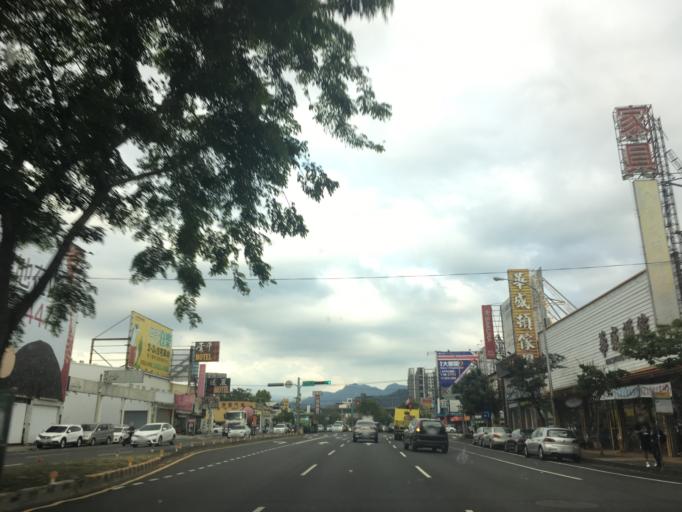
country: TW
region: Taiwan
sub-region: Taichung City
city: Taichung
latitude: 24.1643
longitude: 120.7139
